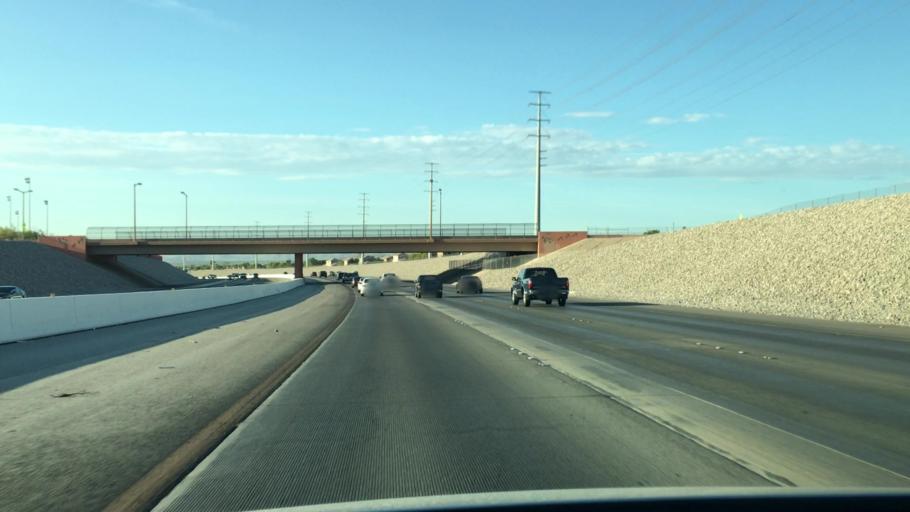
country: US
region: Nevada
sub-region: Clark County
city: Summerlin South
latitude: 36.1309
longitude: -115.3355
